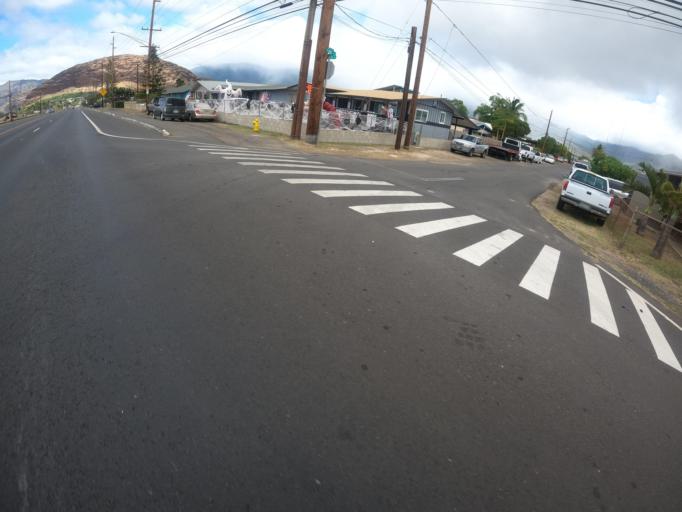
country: US
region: Hawaii
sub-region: Honolulu County
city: Ma'ili
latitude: 21.4183
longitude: -158.1772
